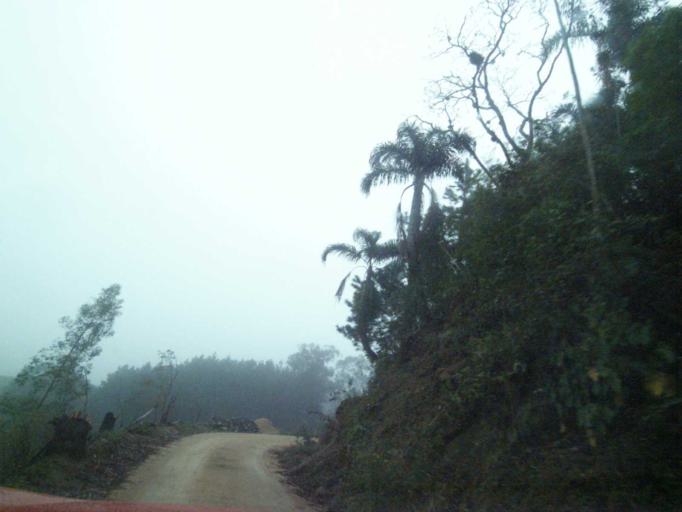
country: BR
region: Santa Catarina
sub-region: Anitapolis
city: Anitapolis
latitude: -27.9136
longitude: -49.1047
